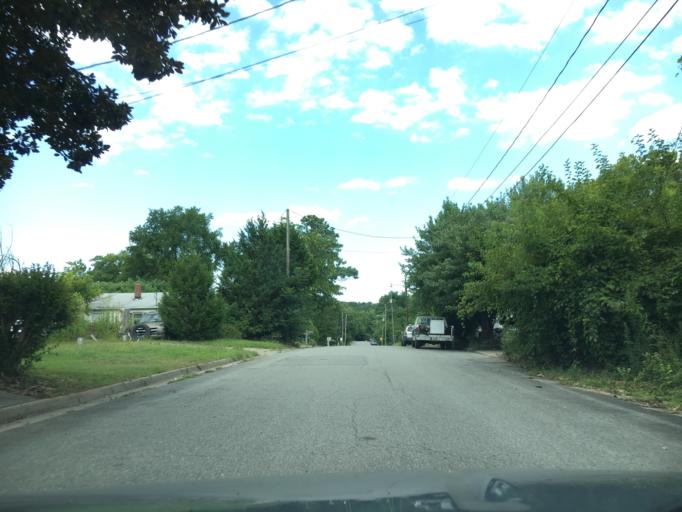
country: US
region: Virginia
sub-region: Halifax County
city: South Boston
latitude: 36.7145
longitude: -78.8990
